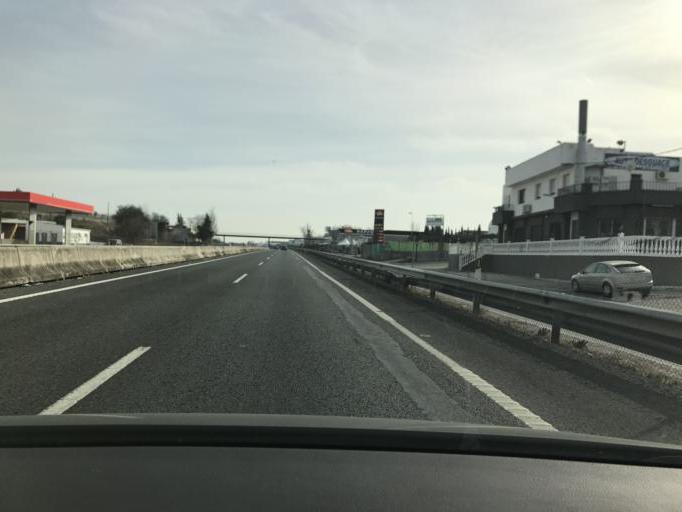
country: ES
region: Andalusia
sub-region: Provincia de Granada
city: Moraleda de Zafayona
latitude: 37.1859
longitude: -3.9601
